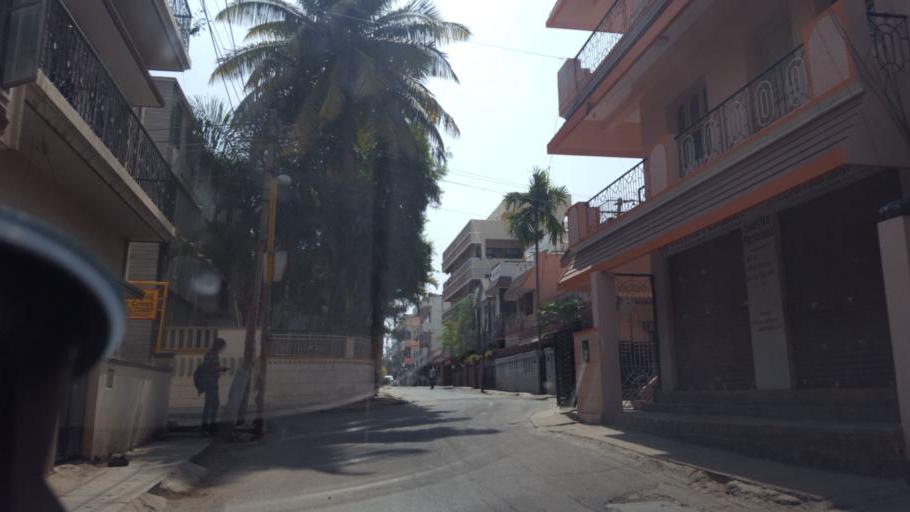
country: IN
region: Karnataka
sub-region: Bangalore Urban
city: Bangalore
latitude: 12.9752
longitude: 77.6735
